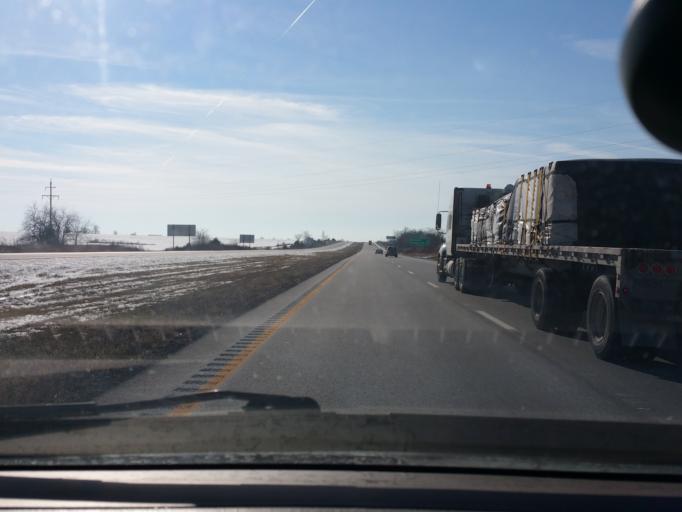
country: US
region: Missouri
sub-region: Clinton County
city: Cameron
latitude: 39.8437
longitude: -94.1812
